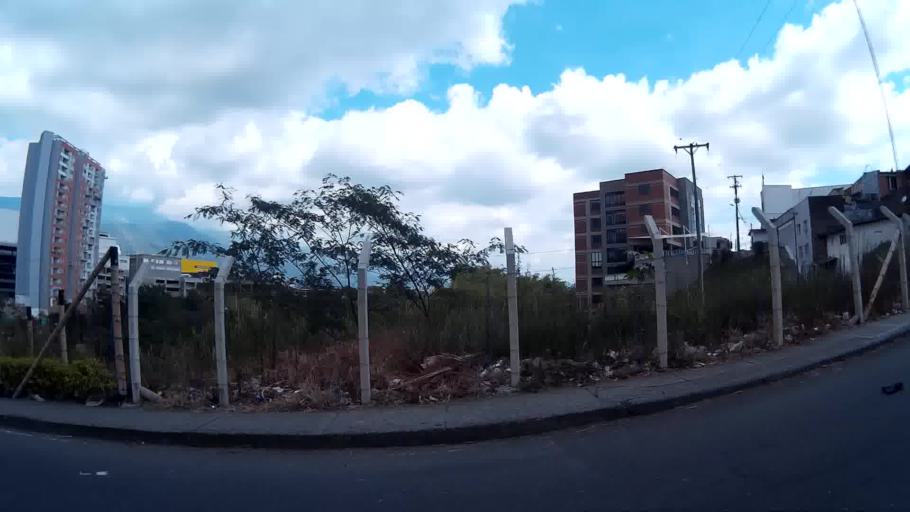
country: CO
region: Quindio
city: Armenia
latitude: 4.5422
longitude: -75.6626
